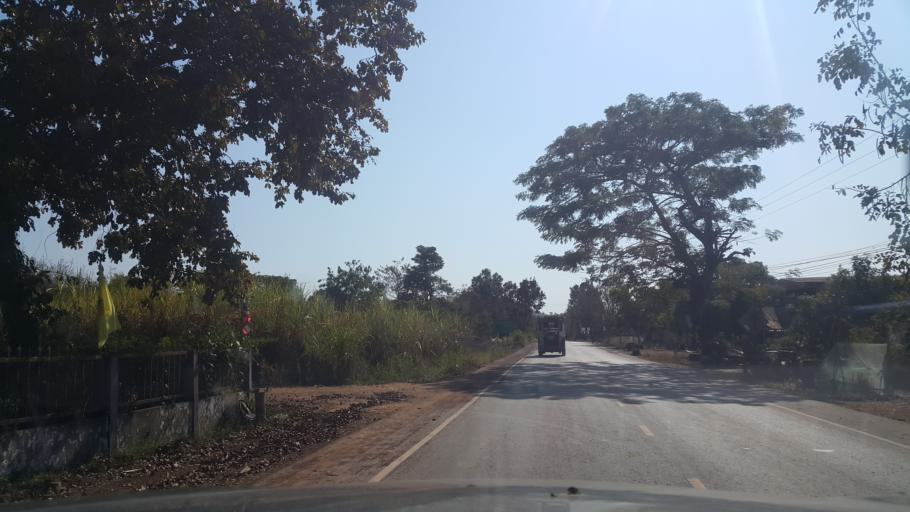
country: TH
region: Changwat Udon Thani
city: Ban Dung
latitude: 17.7024
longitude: 103.3870
